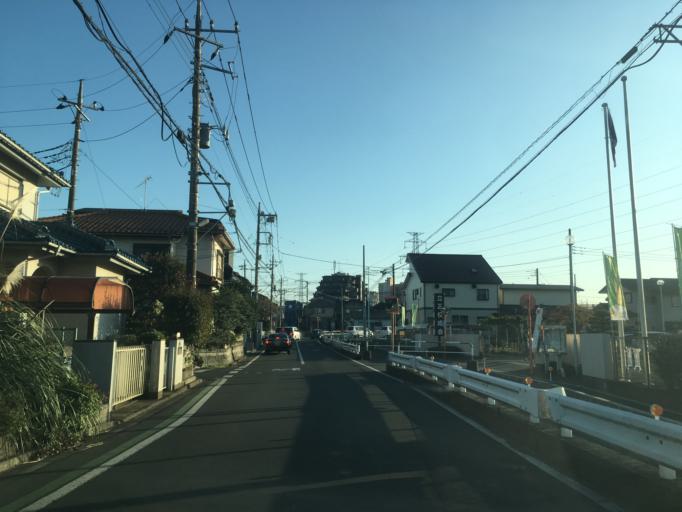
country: JP
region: Saitama
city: Tokorozawa
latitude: 35.8102
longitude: 139.4390
